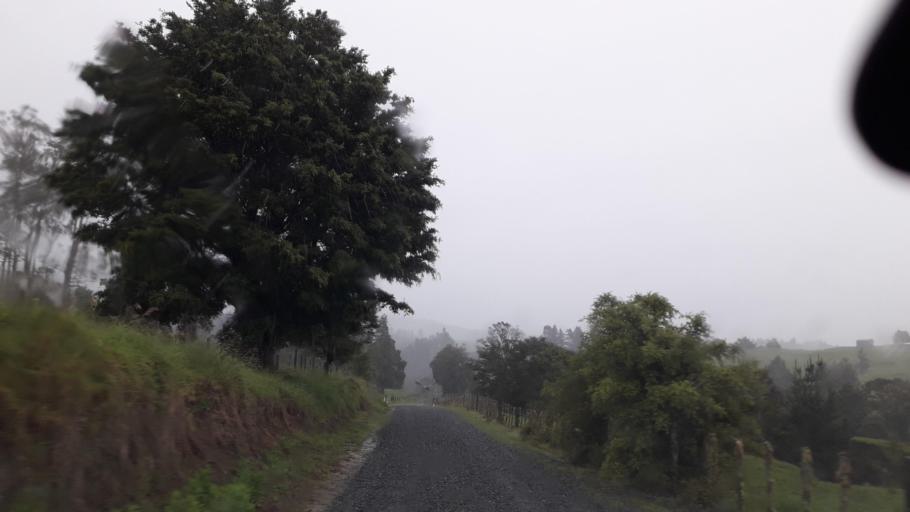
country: NZ
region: Northland
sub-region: Far North District
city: Waimate North
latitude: -35.1548
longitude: 173.7155
